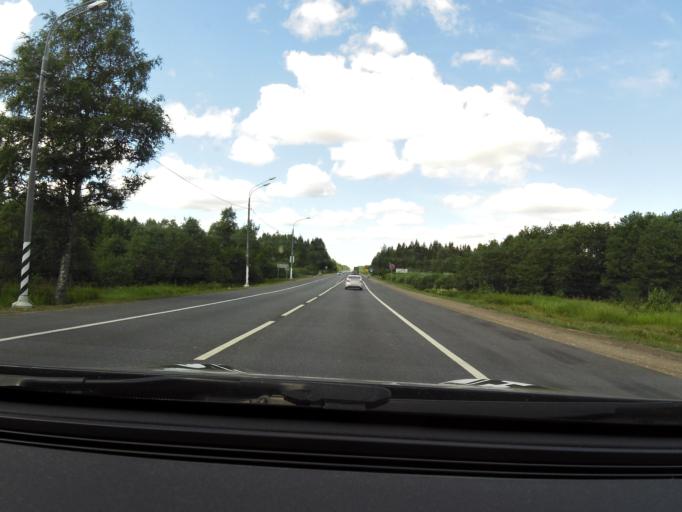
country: RU
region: Tverskaya
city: Kuzhenkino
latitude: 57.7293
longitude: 34.0579
